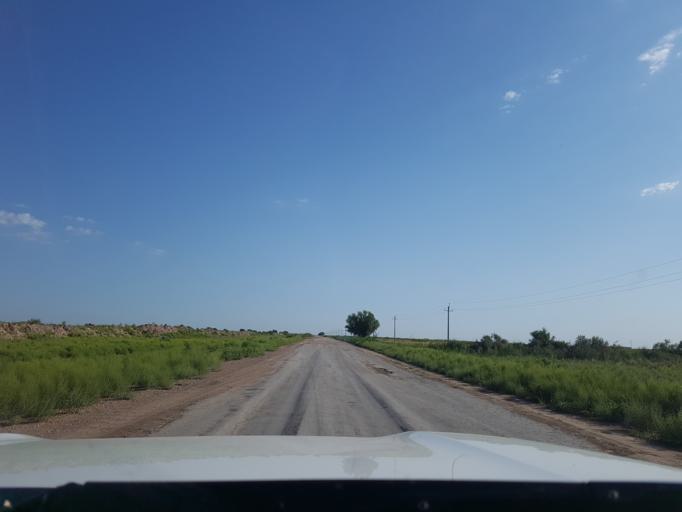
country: TM
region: Dasoguz
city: Koeneuergench
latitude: 41.9202
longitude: 58.7115
